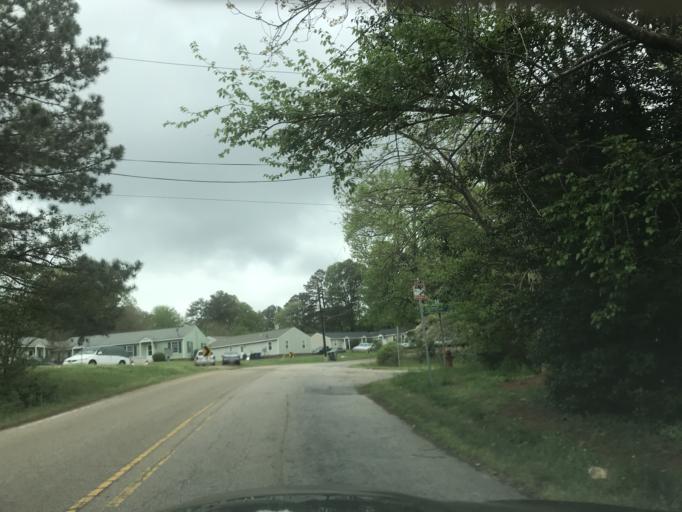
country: US
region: North Carolina
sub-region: Wake County
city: Raleigh
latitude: 35.7466
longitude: -78.6567
